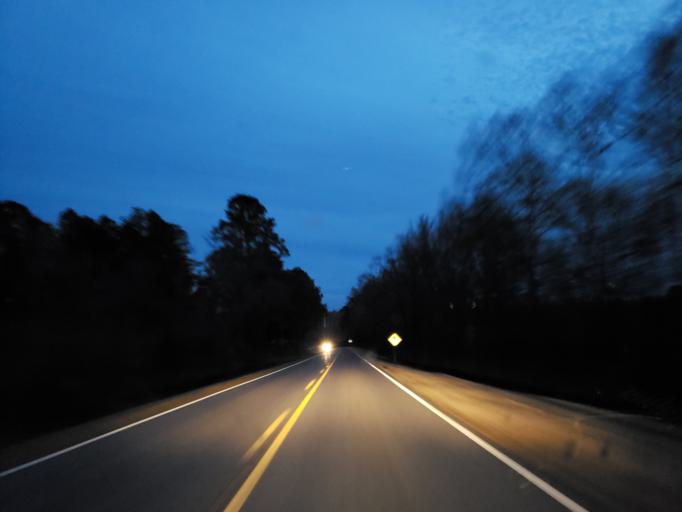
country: US
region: Alabama
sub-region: Greene County
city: Eutaw
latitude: 32.8731
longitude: -87.9284
